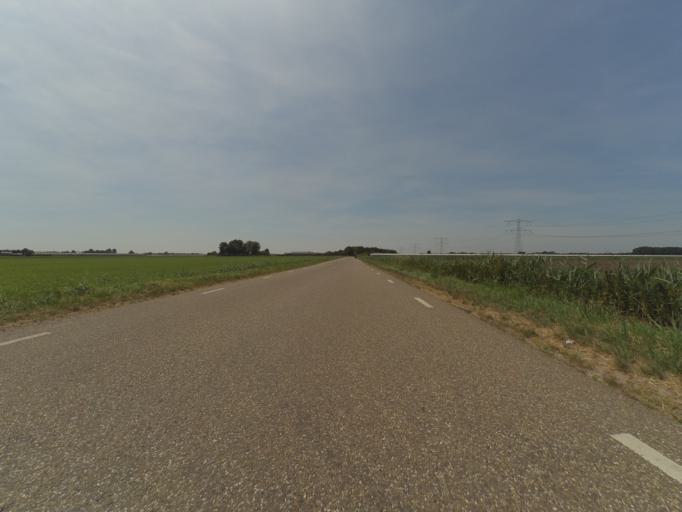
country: NL
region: North Brabant
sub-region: Gemeente Steenbergen
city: Kruisland
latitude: 51.5512
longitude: 4.3749
